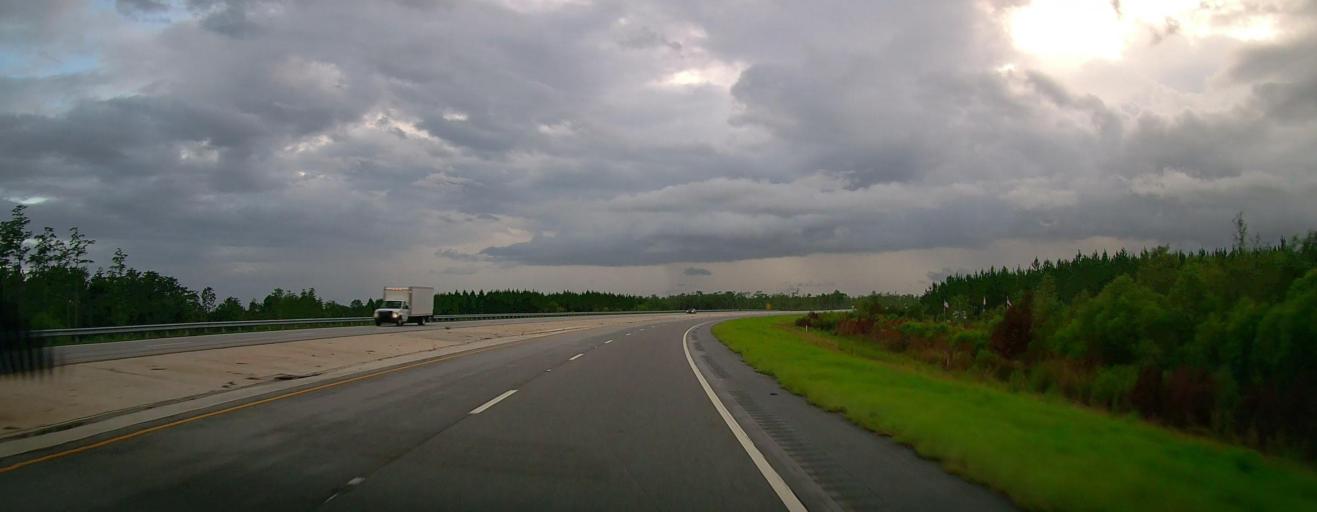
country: US
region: Georgia
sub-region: Ware County
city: Deenwood
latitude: 31.1510
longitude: -82.4463
